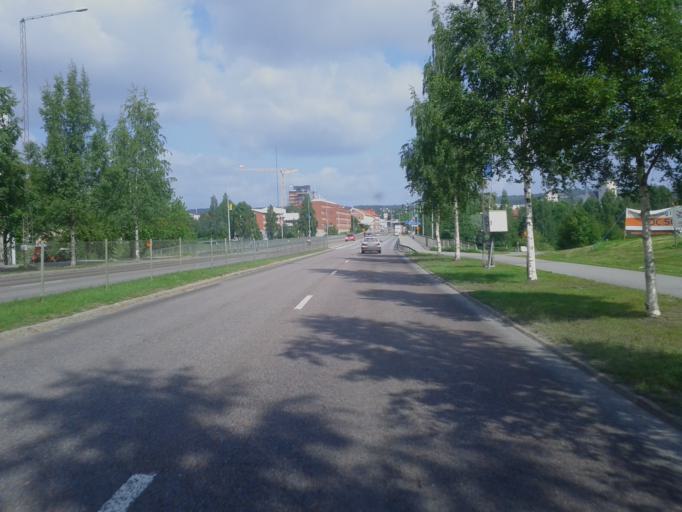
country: SE
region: Vaesterbotten
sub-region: Skelleftea Kommun
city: Skelleftea
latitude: 64.7456
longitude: 20.9597
